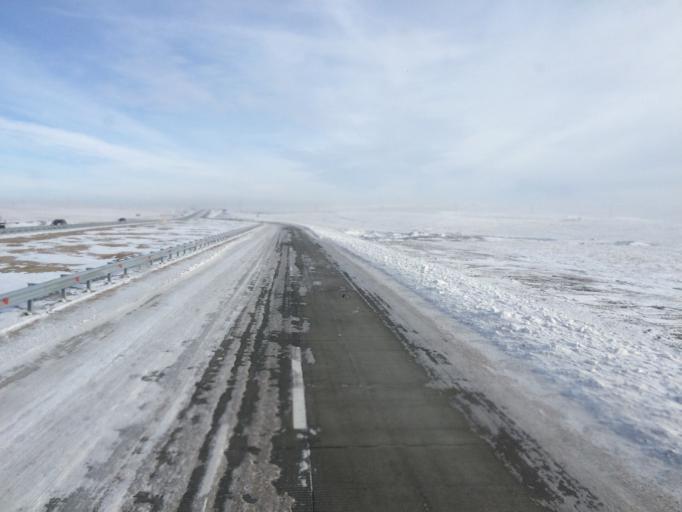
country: KZ
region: Zhambyl
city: Georgiyevka
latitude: 43.3498
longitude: 74.5439
